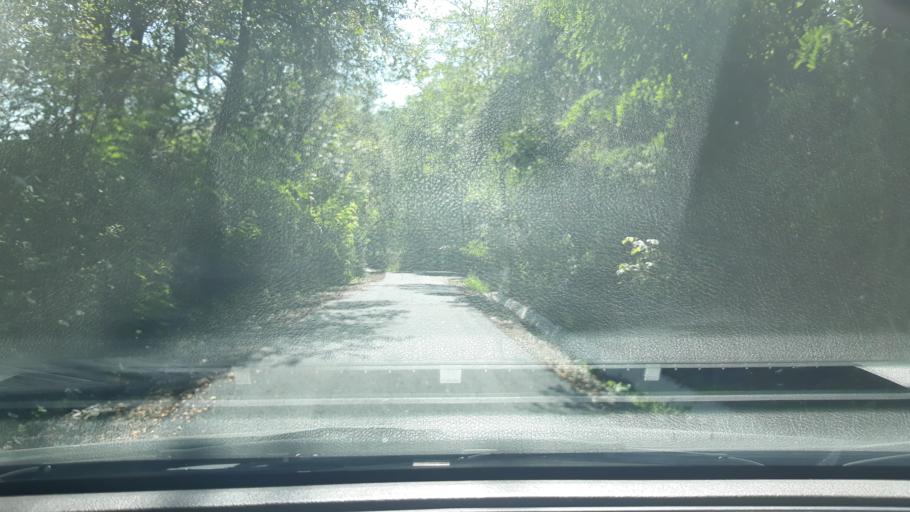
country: RO
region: Salaj
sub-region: Comuna Dobrin
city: Dobrin
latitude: 47.2932
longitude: 23.0840
